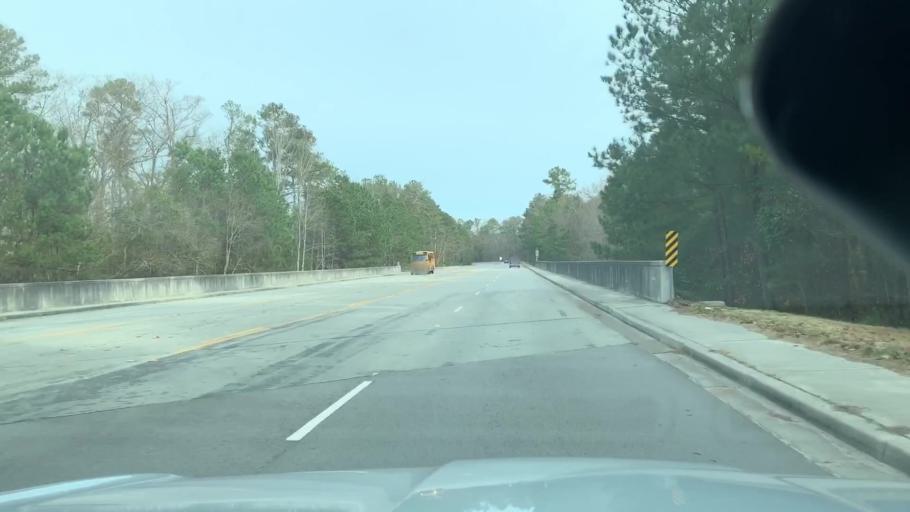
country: US
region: South Carolina
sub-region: Richland County
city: Dentsville
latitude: 34.0632
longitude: -80.9479
